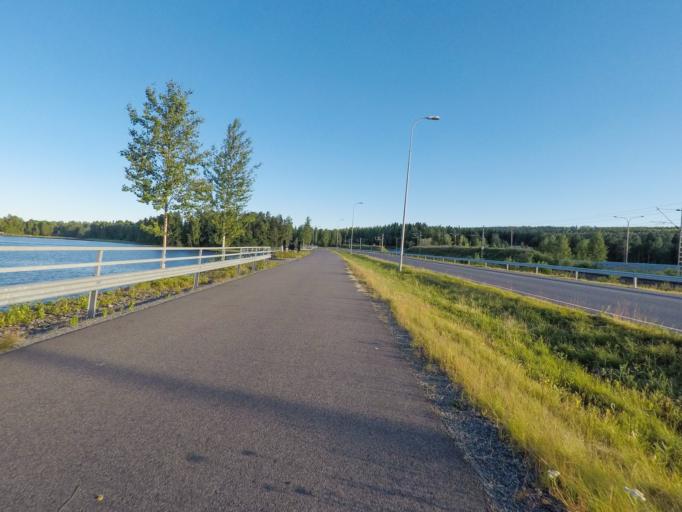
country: FI
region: Northern Savo
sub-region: Kuopio
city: Kuopio
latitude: 62.9398
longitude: 27.6681
